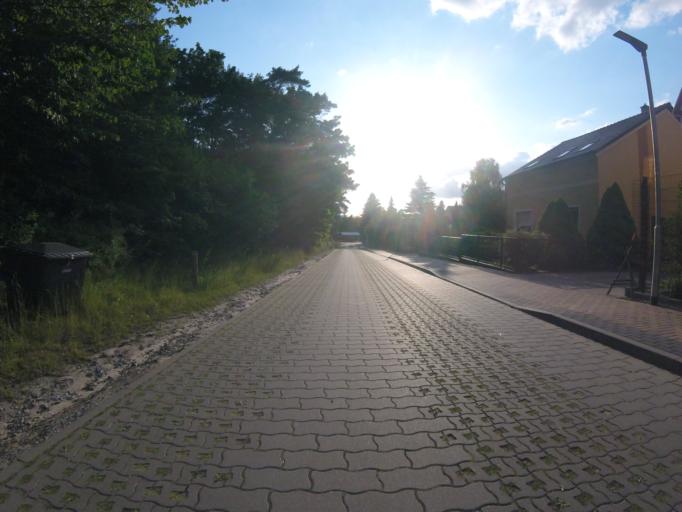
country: DE
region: Brandenburg
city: Schwerin
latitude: 52.1991
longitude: 13.5879
